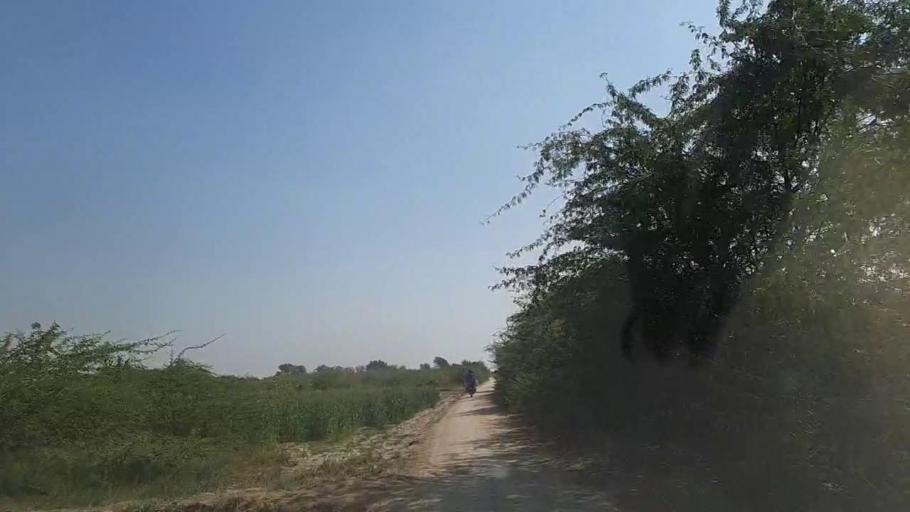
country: PK
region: Sindh
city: Digri
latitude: 25.1658
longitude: 69.1726
